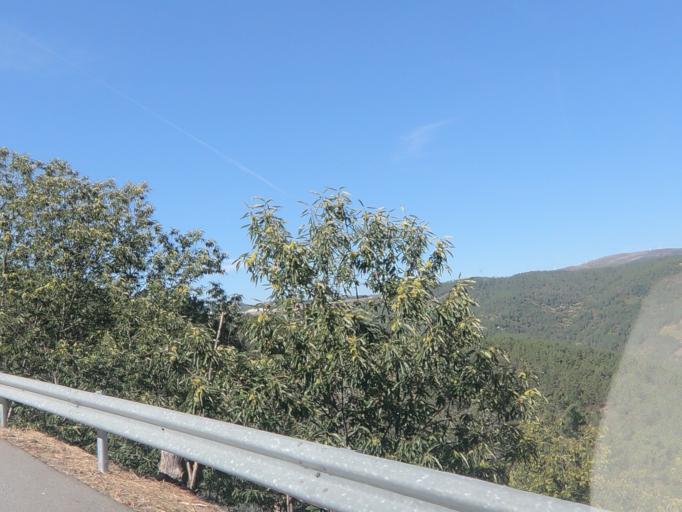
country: PT
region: Vila Real
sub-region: Santa Marta de Penaguiao
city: Santa Marta de Penaguiao
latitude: 41.2505
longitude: -7.8440
